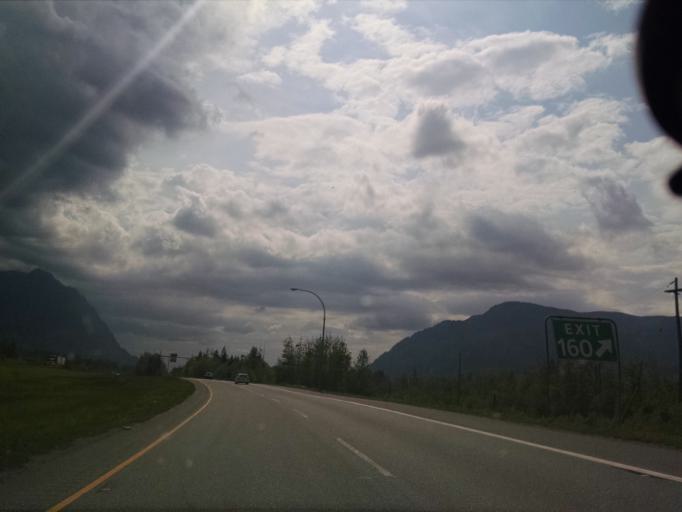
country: CA
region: British Columbia
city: Hope
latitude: 49.3559
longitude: -121.5782
